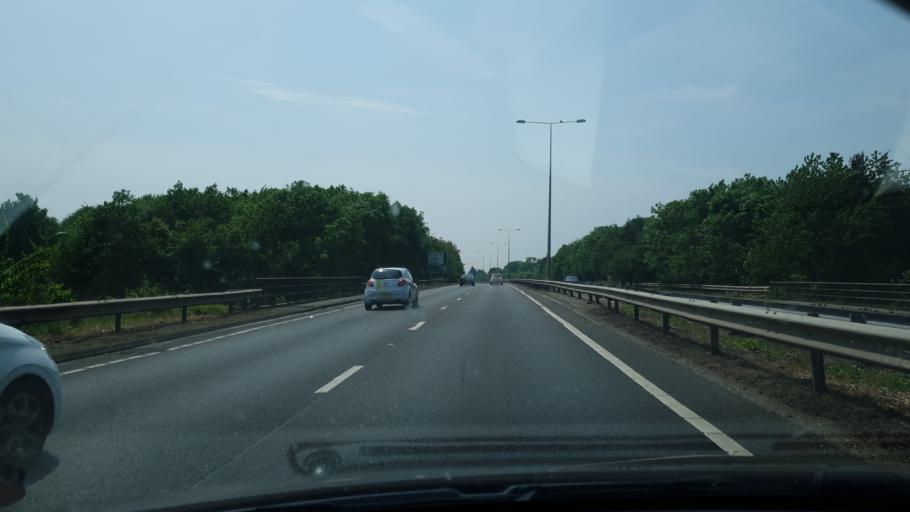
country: GB
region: England
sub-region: Suffolk
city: Capel Saint Mary
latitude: 52.0149
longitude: 1.0704
